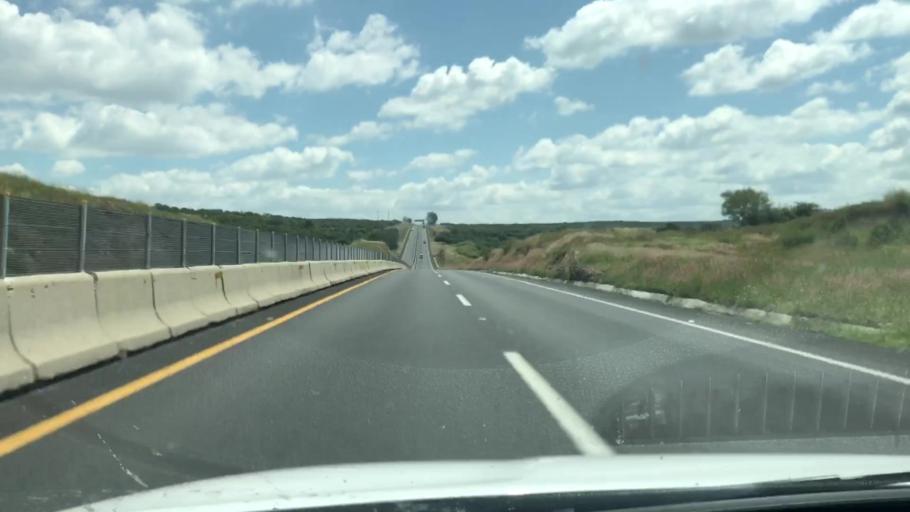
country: MX
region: Guanajuato
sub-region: Leon
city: Rizos de la Joya (Rizos del Saucillo)
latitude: 21.1284
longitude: -101.8181
